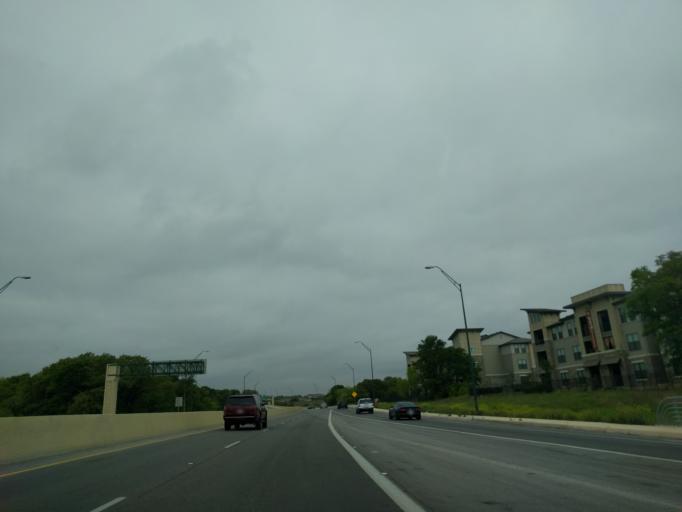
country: US
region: Texas
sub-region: Bexar County
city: Castle Hills
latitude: 29.5590
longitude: -98.5012
